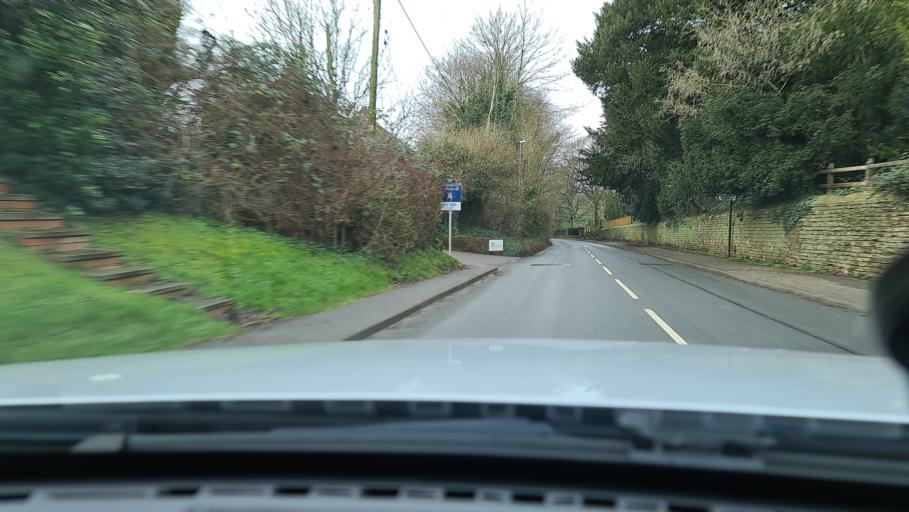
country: GB
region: England
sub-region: Oxfordshire
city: Adderbury
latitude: 52.0718
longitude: -1.2753
